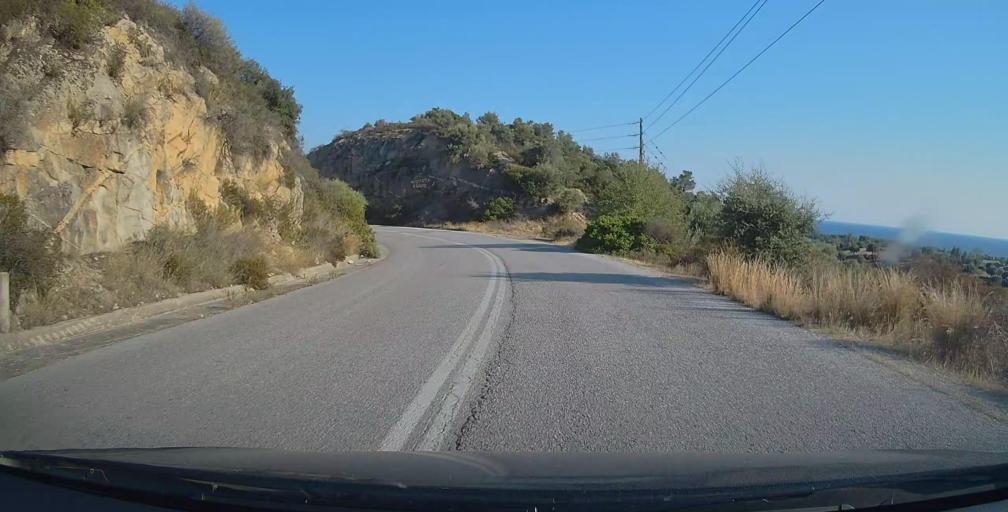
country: GR
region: Central Macedonia
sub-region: Nomos Chalkidikis
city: Sykia
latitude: 40.0065
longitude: 23.8797
